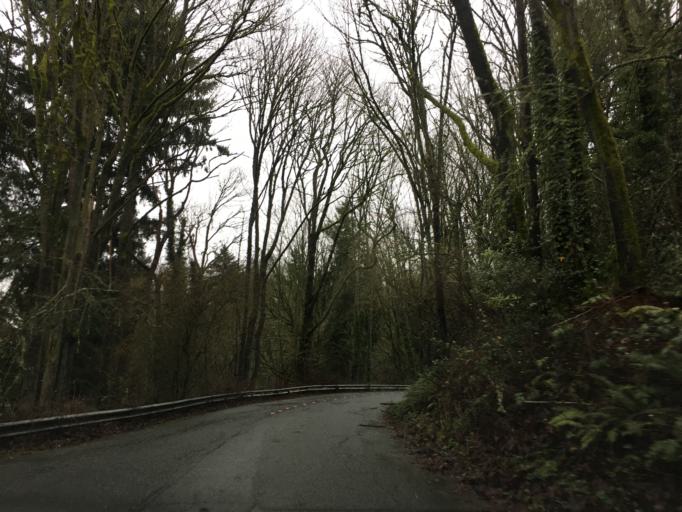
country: US
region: Washington
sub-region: King County
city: Seattle
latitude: 47.6383
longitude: -122.3112
